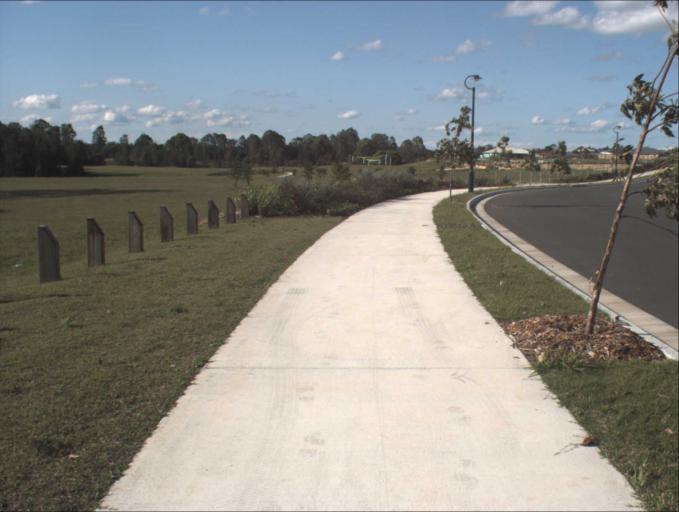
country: AU
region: Queensland
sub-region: Logan
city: Chambers Flat
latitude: -27.7778
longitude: 153.0965
